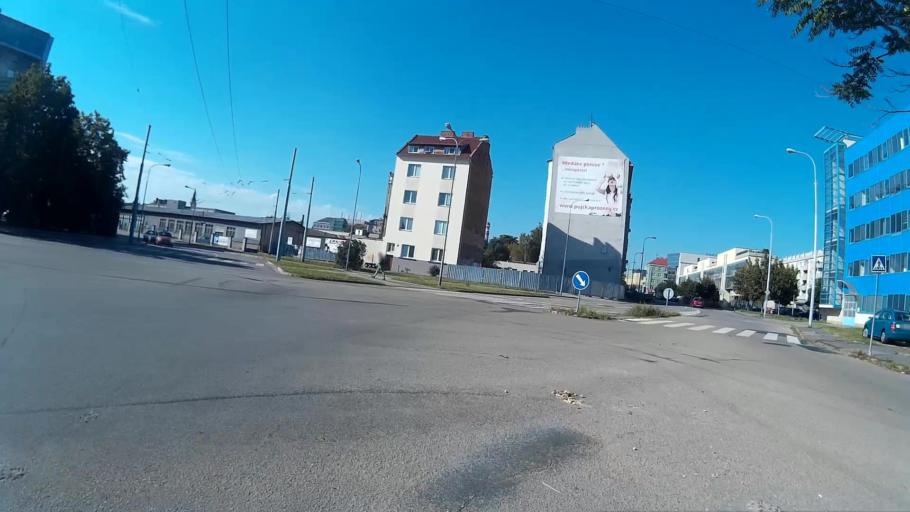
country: CZ
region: South Moravian
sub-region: Mesto Brno
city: Brno
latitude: 49.1889
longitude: 16.6258
